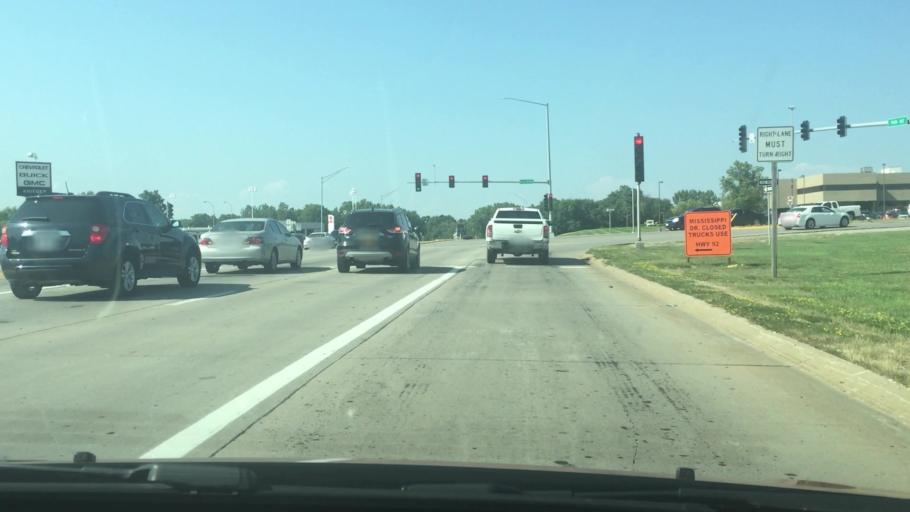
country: US
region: Iowa
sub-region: Muscatine County
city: Muscatine
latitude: 41.4532
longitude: -91.0300
